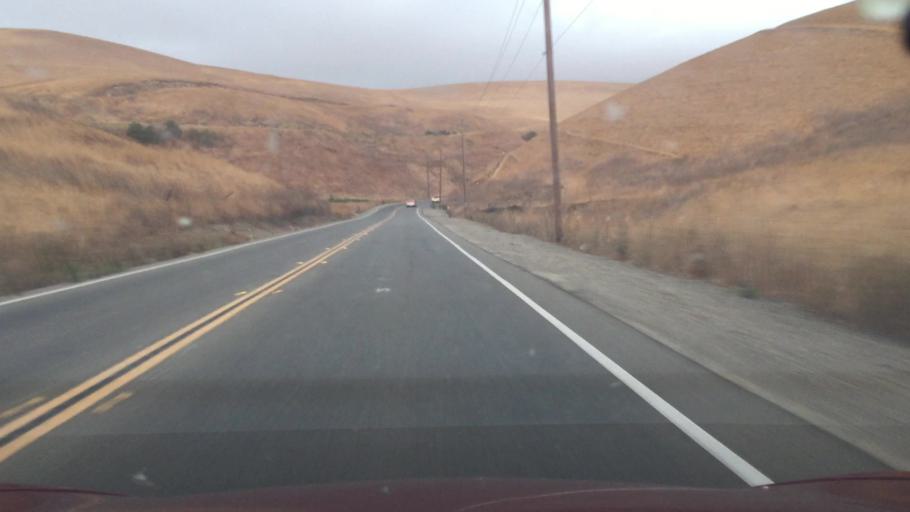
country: US
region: California
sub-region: San Joaquin County
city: Mountain House
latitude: 37.7444
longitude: -121.6455
